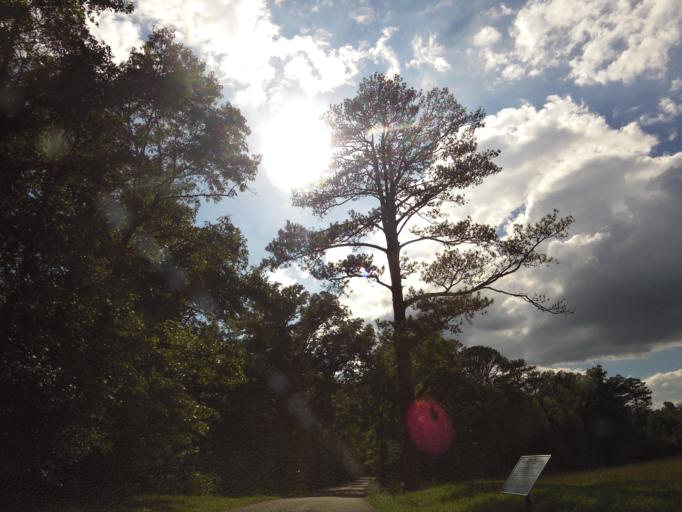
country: US
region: Georgia
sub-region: Walker County
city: Chickamauga
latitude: 34.9011
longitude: -85.2625
